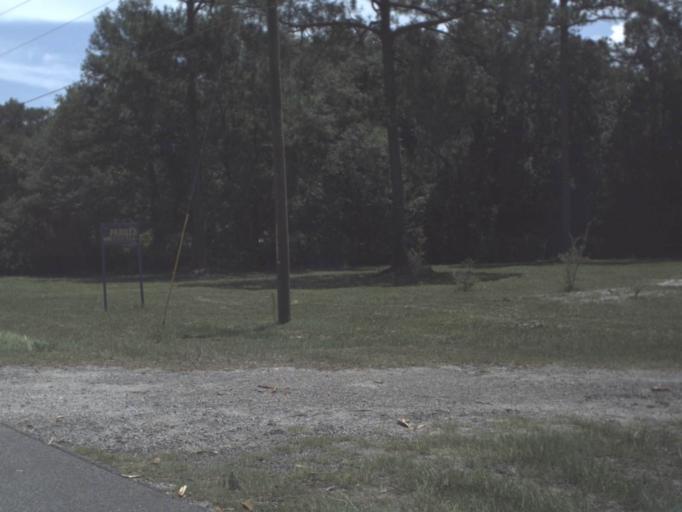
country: US
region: Florida
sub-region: Taylor County
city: Perry
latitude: 30.0969
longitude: -83.6285
